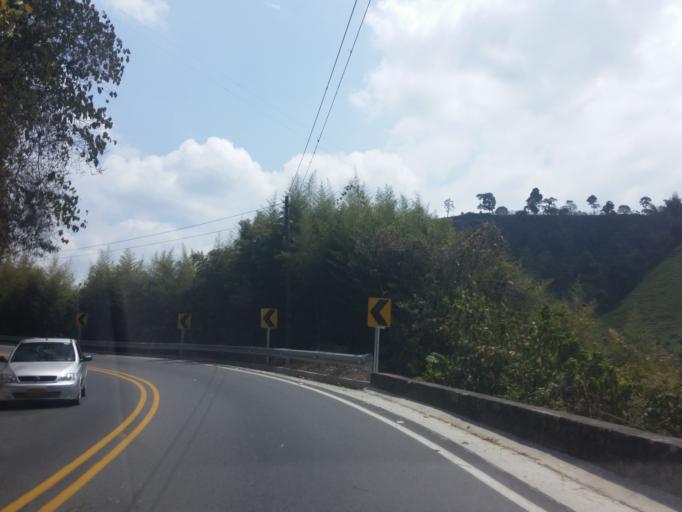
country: CO
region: Caldas
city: Chinchina
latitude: 4.9868
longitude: -75.5820
